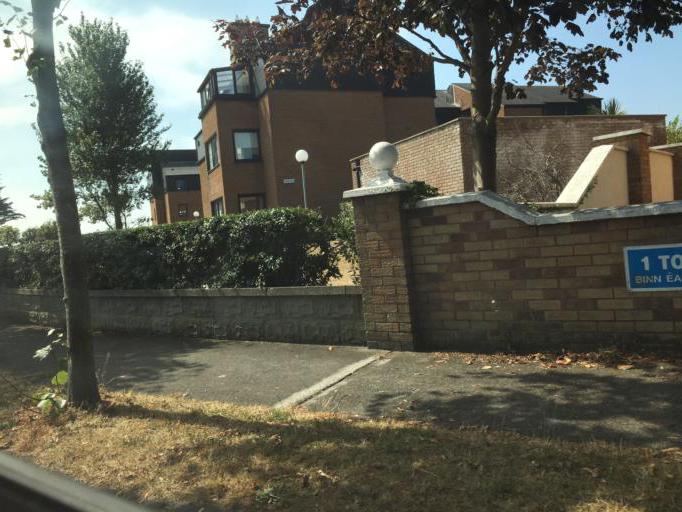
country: IE
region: Leinster
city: Sutton
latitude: 53.3900
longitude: -6.1200
